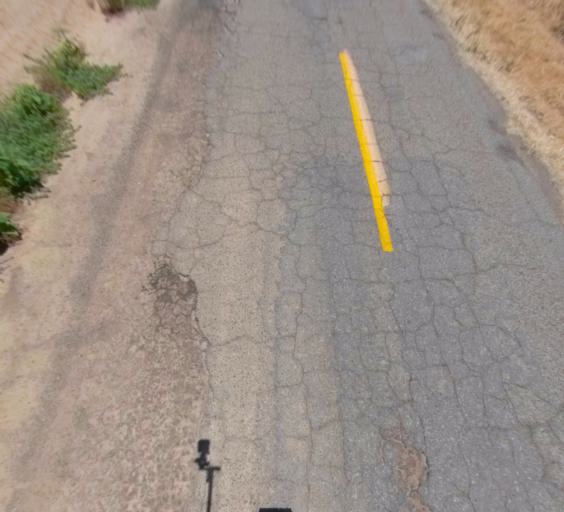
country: US
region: California
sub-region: Fresno County
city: Fresno
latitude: 36.8591
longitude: -119.8245
